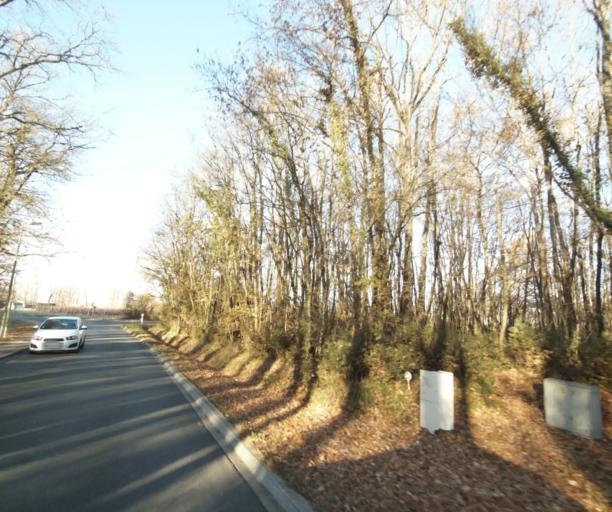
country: FR
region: Poitou-Charentes
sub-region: Departement de la Charente-Maritime
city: Fontcouverte
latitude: 45.7660
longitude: -0.6090
